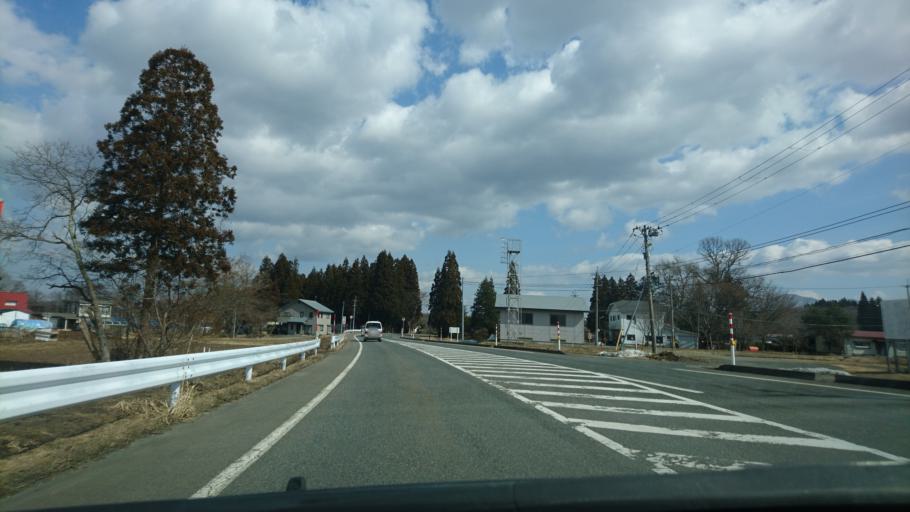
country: JP
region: Iwate
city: Shizukuishi
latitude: 39.6474
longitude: 140.9487
